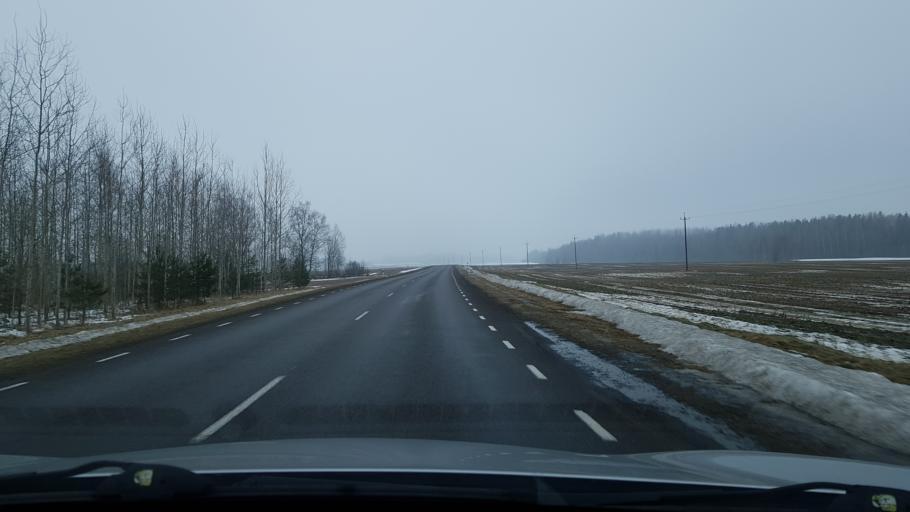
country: EE
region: Valgamaa
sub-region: Torva linn
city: Torva
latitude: 58.0998
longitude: 26.0114
